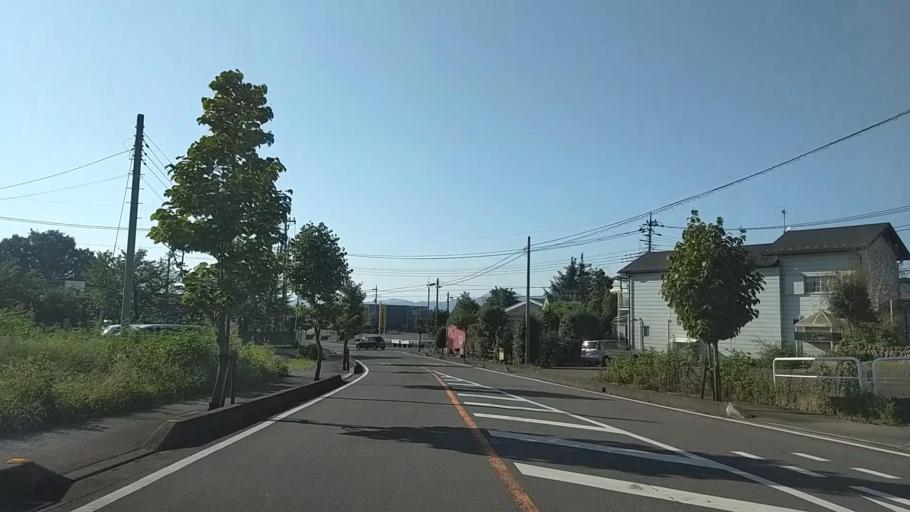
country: JP
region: Gunma
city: Annaka
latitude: 36.3188
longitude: 138.8763
